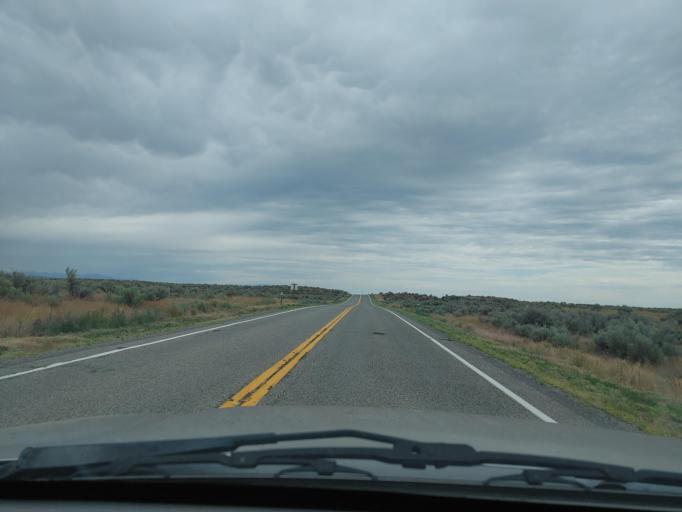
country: US
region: Idaho
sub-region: Lincoln County
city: Shoshone
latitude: 43.0717
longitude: -114.1106
